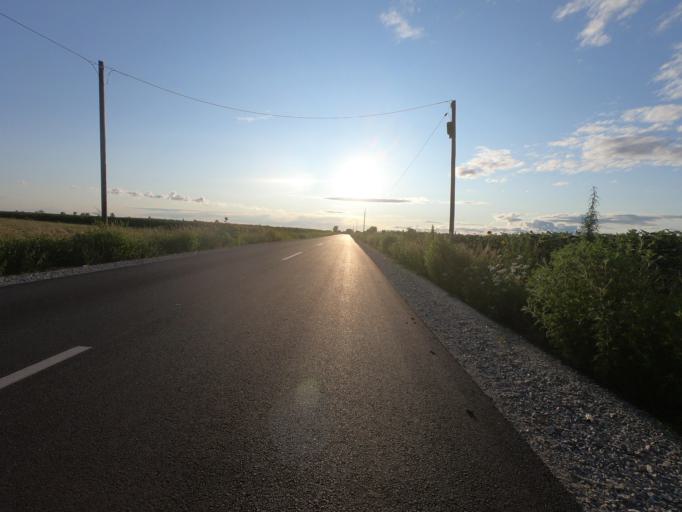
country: HU
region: Heves
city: Szihalom
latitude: 47.7117
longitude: 20.4979
